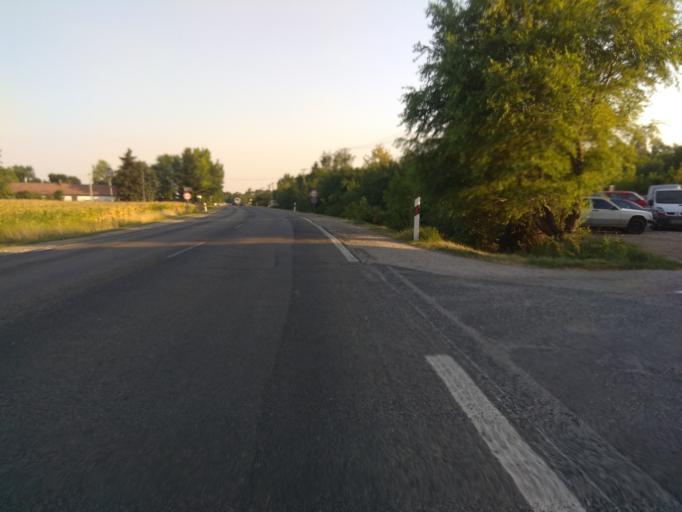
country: HU
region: Borsod-Abauj-Zemplen
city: Nyekladhaza
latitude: 47.9747
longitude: 20.8301
